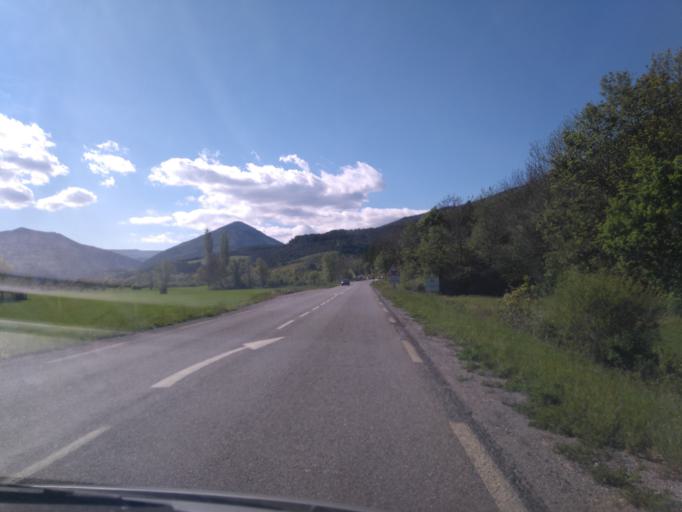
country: FR
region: Provence-Alpes-Cote d'Azur
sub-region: Departement des Hautes-Alpes
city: Veynes
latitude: 44.5629
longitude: 5.7620
